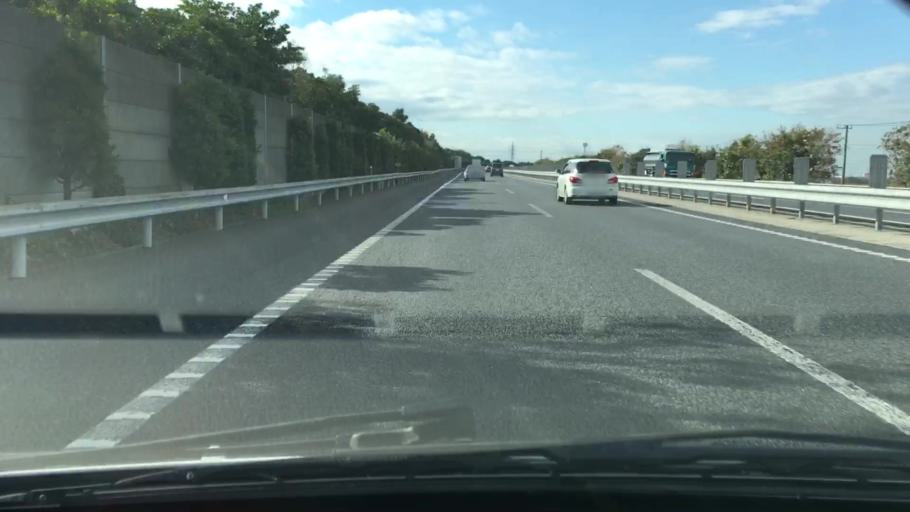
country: JP
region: Chiba
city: Ichihara
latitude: 35.5187
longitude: 140.1210
